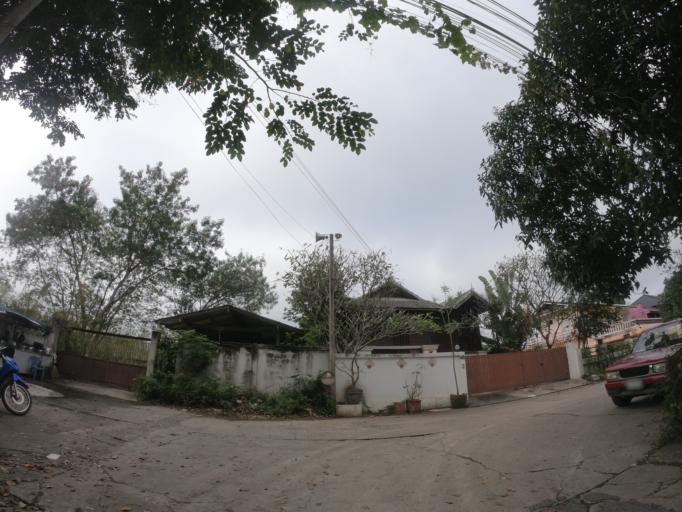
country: TH
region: Chiang Mai
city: Chiang Mai
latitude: 18.7588
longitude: 98.9773
